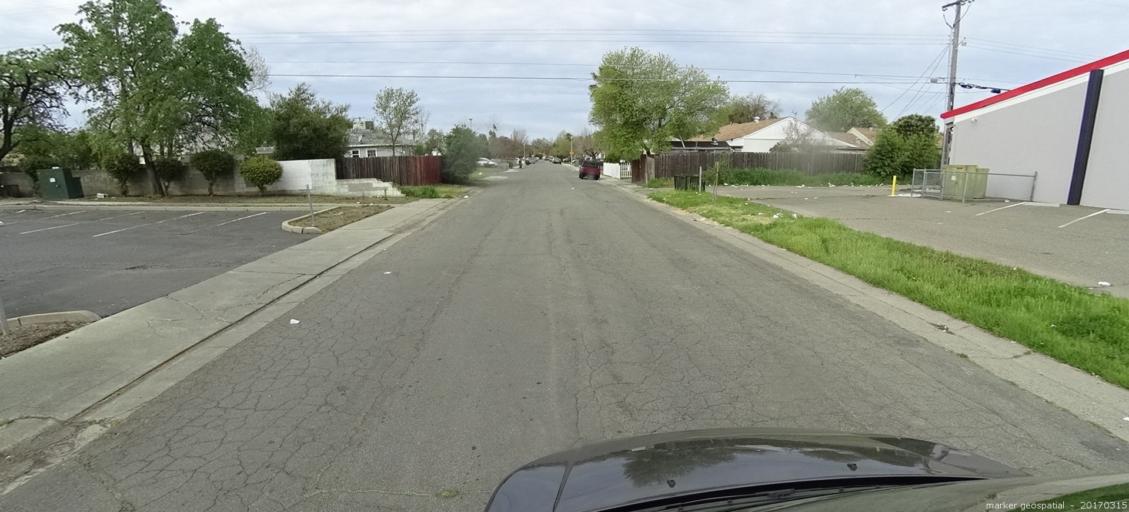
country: US
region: California
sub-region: Sacramento County
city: Parkway
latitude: 38.5188
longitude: -121.4998
